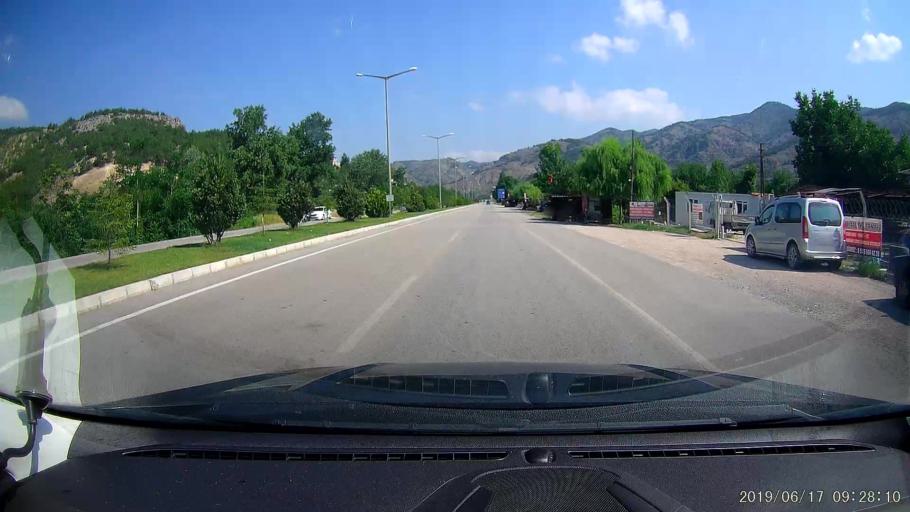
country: TR
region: Amasya
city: Amasya
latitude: 40.6852
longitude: 35.8230
